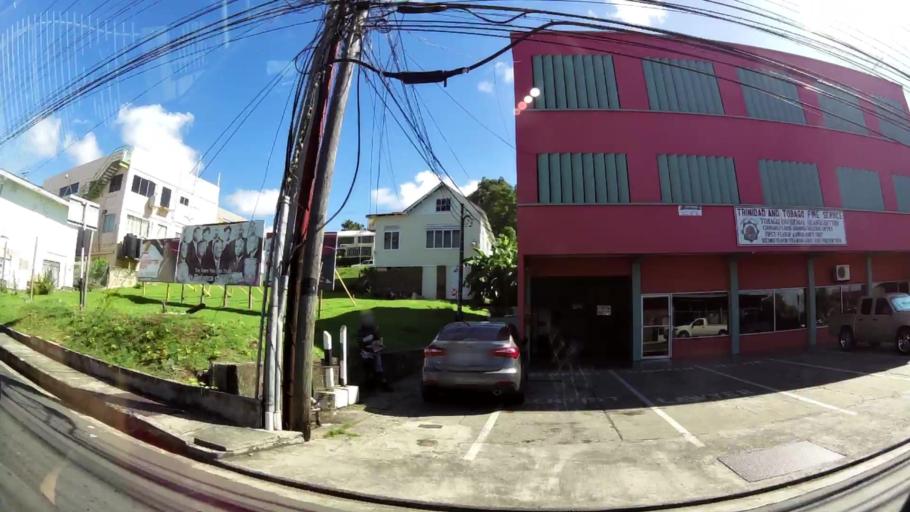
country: TT
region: Tobago
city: Scarborough
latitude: 11.1806
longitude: -60.7329
